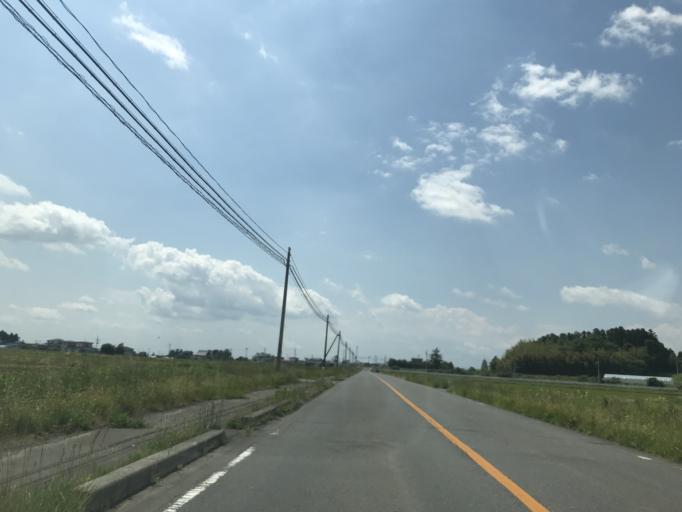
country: JP
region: Miyagi
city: Kogota
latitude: 38.6116
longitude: 141.0212
